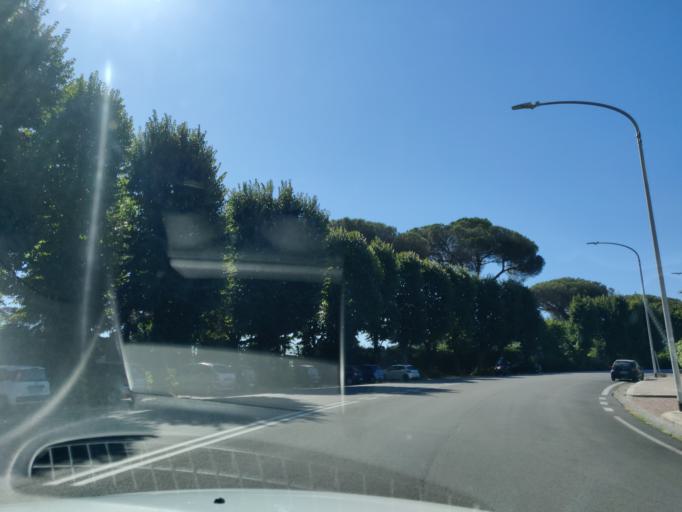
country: IT
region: Latium
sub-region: Citta metropolitana di Roma Capitale
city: Rome
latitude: 41.8366
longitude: 12.4751
